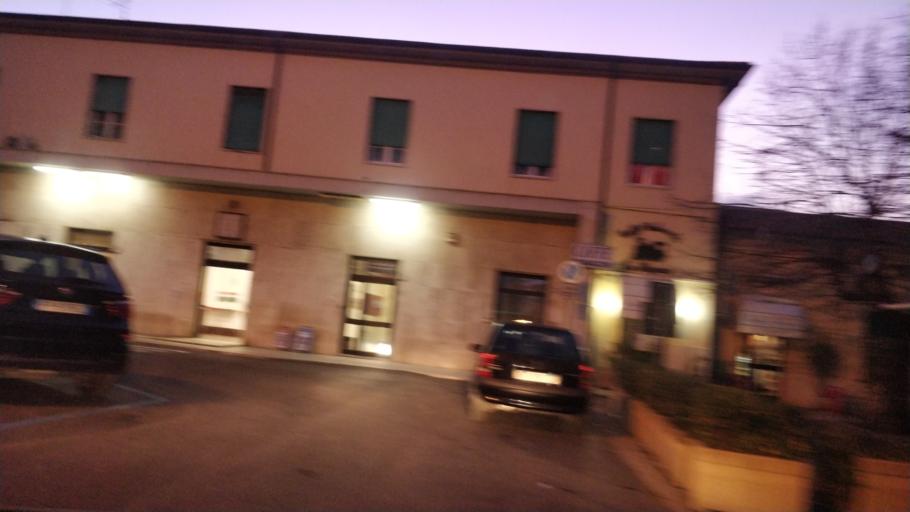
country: IT
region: Tuscany
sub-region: Provincia di Livorno
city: Cecina
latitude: 43.3107
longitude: 10.5147
